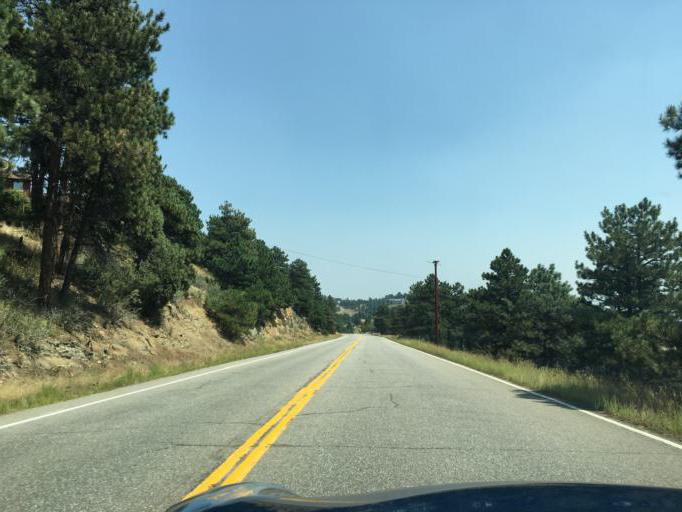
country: US
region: Colorado
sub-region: Jefferson County
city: Genesee
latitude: 39.7093
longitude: -105.2782
